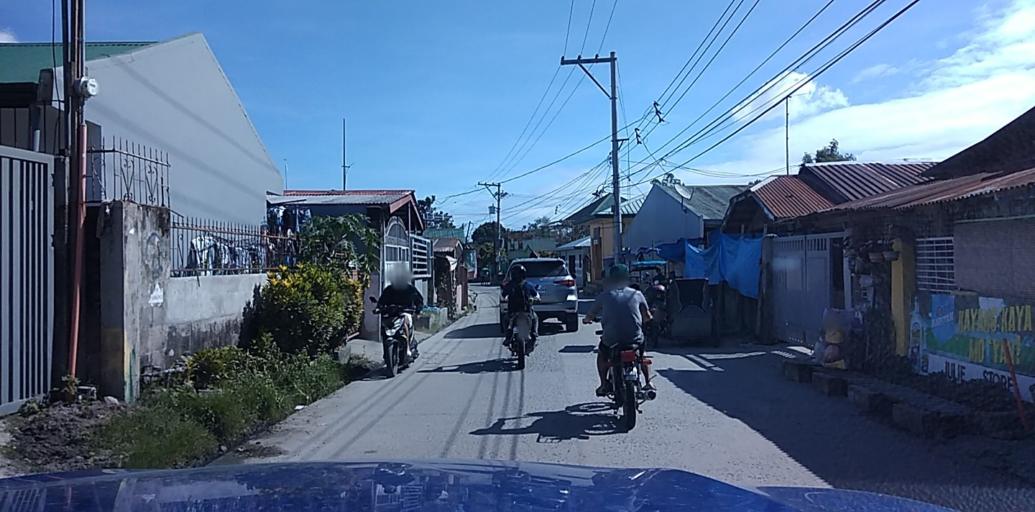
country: PH
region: Central Luzon
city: Santol
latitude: 15.1691
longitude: 120.5116
